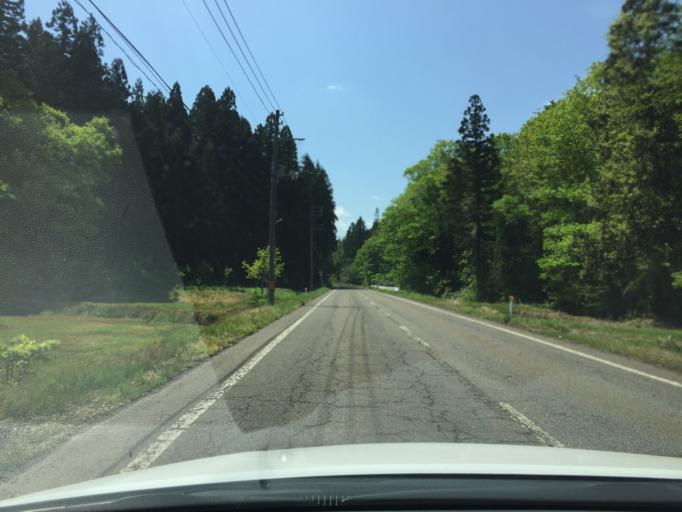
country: JP
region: Niigata
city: Tochio-honcho
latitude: 37.5383
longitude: 139.0919
